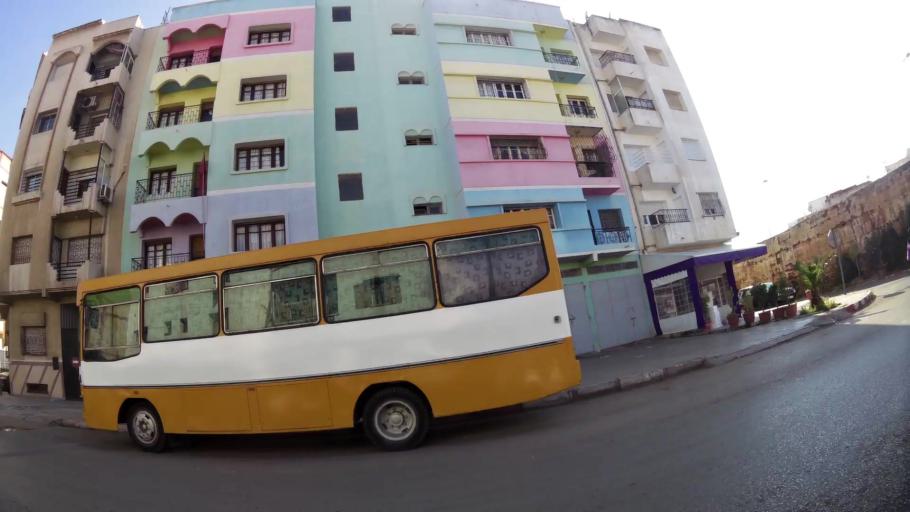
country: MA
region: Rabat-Sale-Zemmour-Zaer
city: Sale
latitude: 34.0465
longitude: -6.8085
